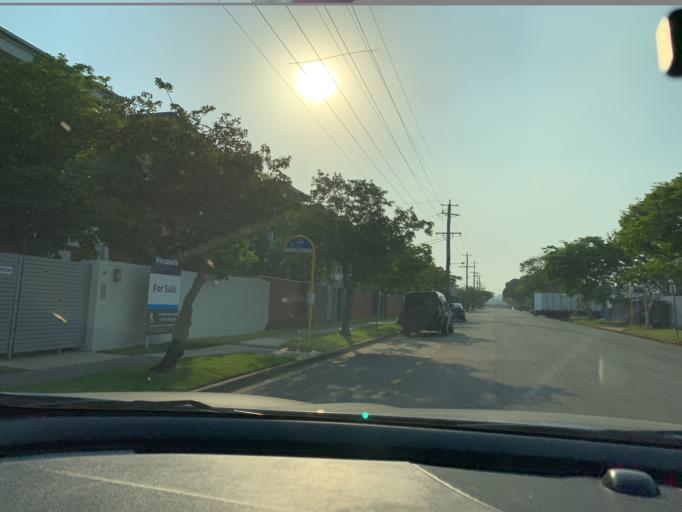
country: AU
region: Queensland
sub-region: Brisbane
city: Ascot
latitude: -27.4290
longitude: 153.0760
